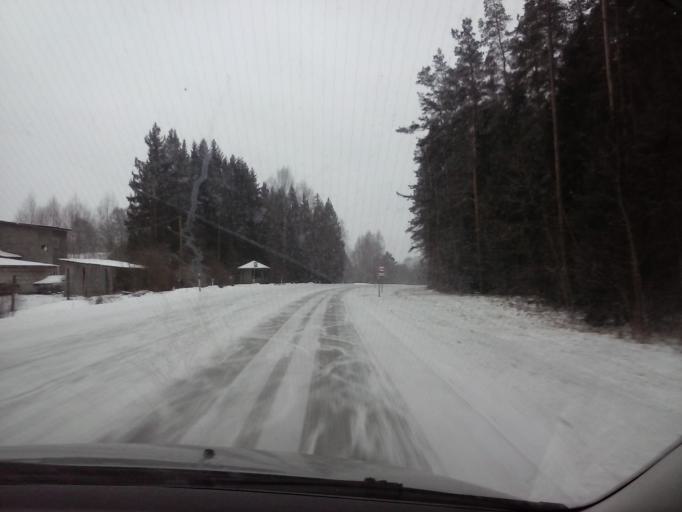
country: EE
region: Valgamaa
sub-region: Torva linn
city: Torva
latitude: 57.9891
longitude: 26.1728
